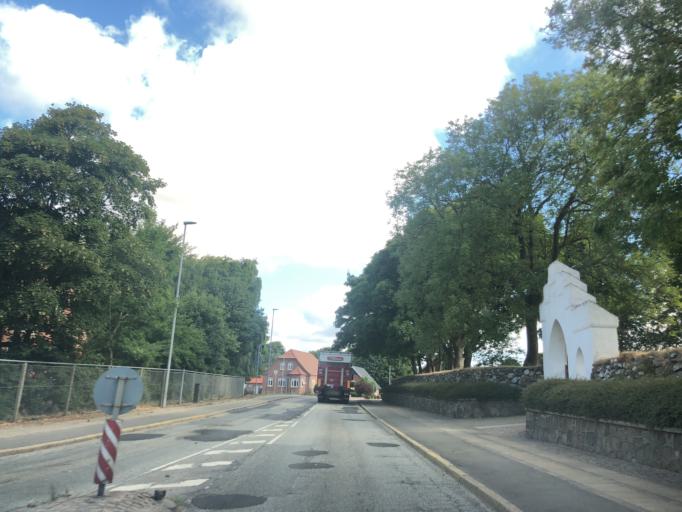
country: DK
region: Central Jutland
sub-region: Skive Kommune
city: Skive
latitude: 56.6495
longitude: 8.9330
